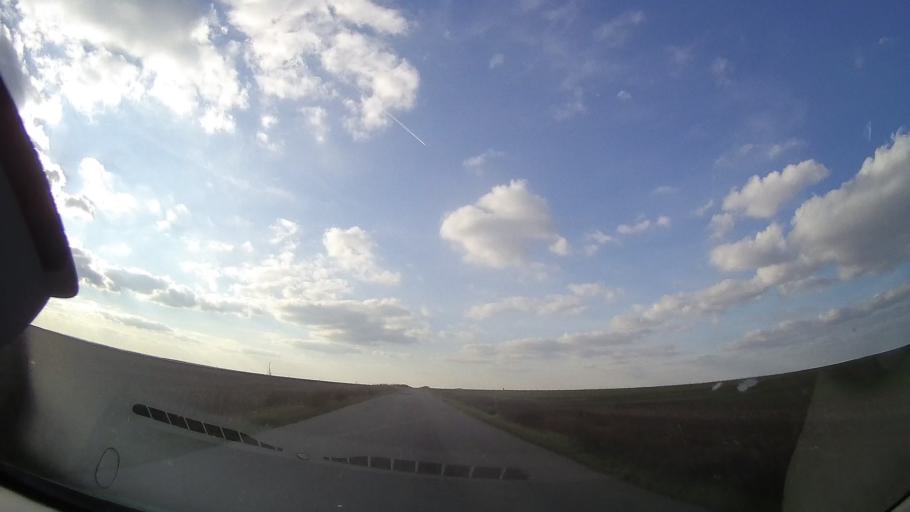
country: RO
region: Constanta
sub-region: Comuna Cerchezu
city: Cerchezu
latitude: 43.8237
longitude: 28.1446
